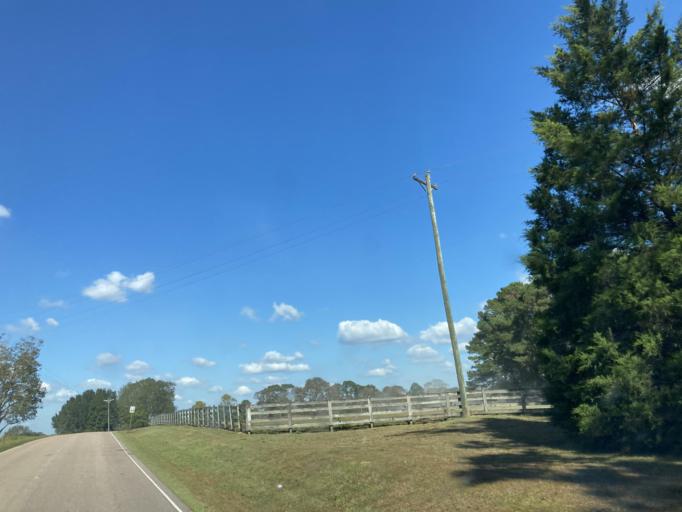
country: US
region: Mississippi
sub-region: Lamar County
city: Sumrall
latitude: 31.2997
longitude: -89.5408
